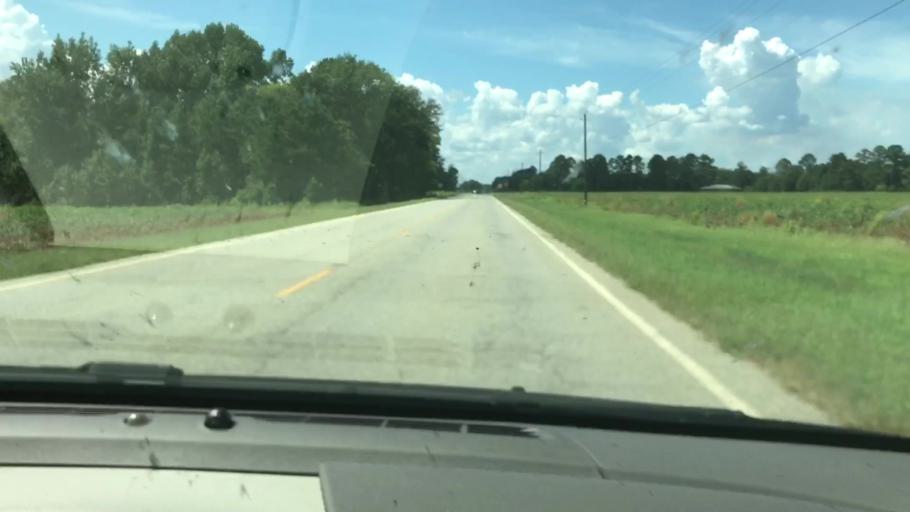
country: US
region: Georgia
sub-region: Quitman County
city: Georgetown
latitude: 31.7585
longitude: -85.0688
